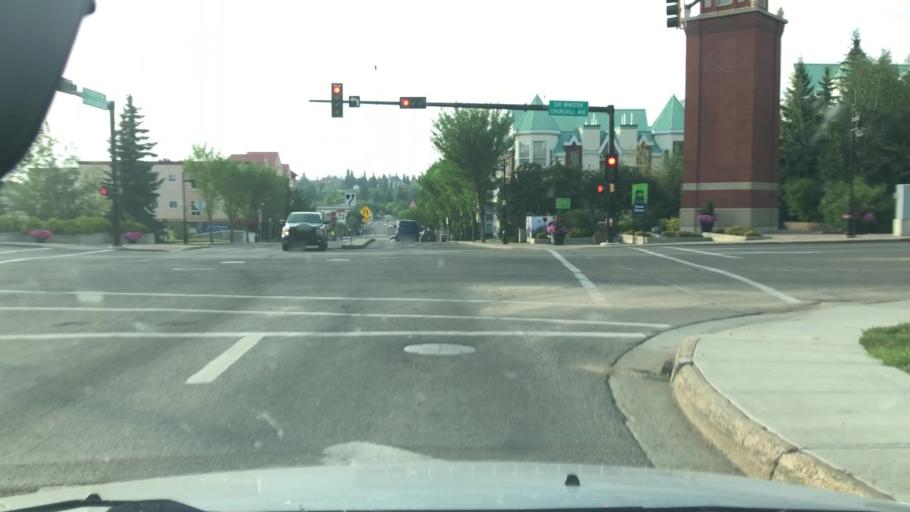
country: CA
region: Alberta
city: St. Albert
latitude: 53.6318
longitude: -113.6232
